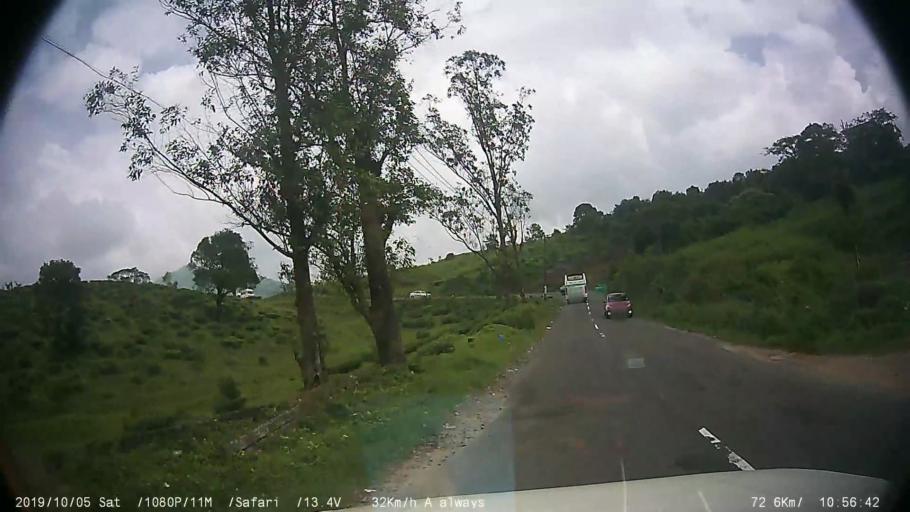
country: IN
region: Kerala
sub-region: Kottayam
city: Erattupetta
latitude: 9.5858
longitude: 76.9694
